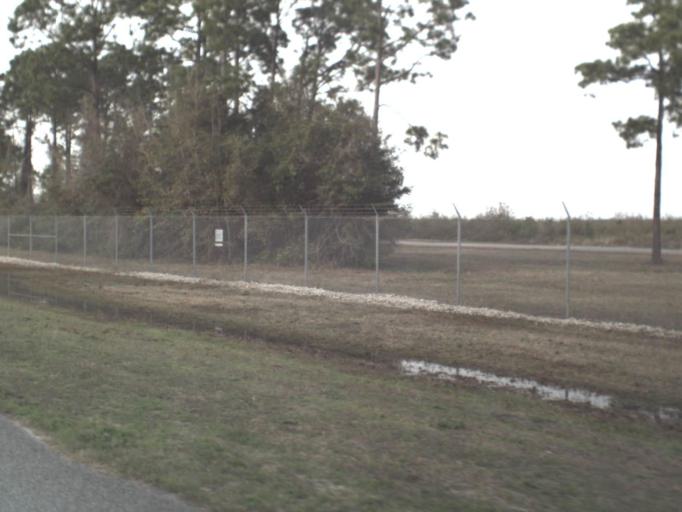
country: US
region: Florida
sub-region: Bay County
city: Tyndall Air Force Base
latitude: 30.0533
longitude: -85.5685
